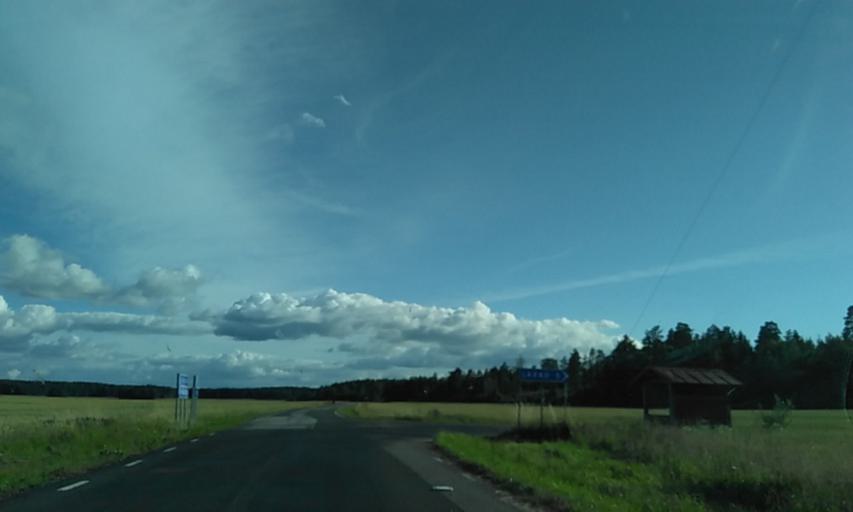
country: SE
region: Vaestra Goetaland
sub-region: Vara Kommun
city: Vara
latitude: 58.3945
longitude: 12.9072
